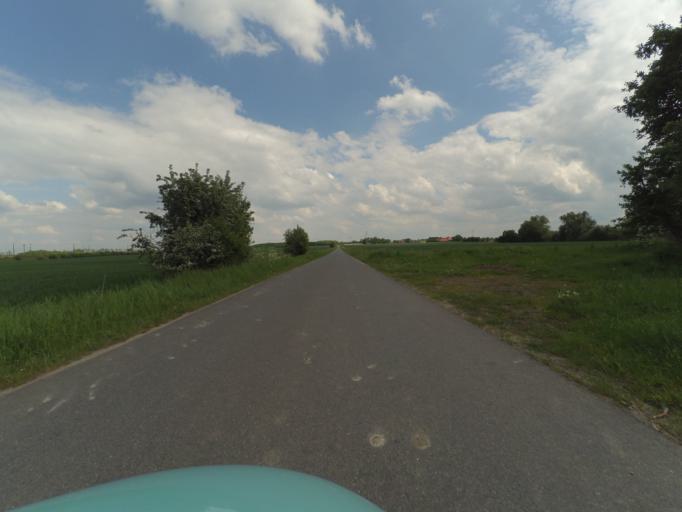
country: DE
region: Lower Saxony
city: Lehrte
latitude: 52.3663
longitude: 10.0018
